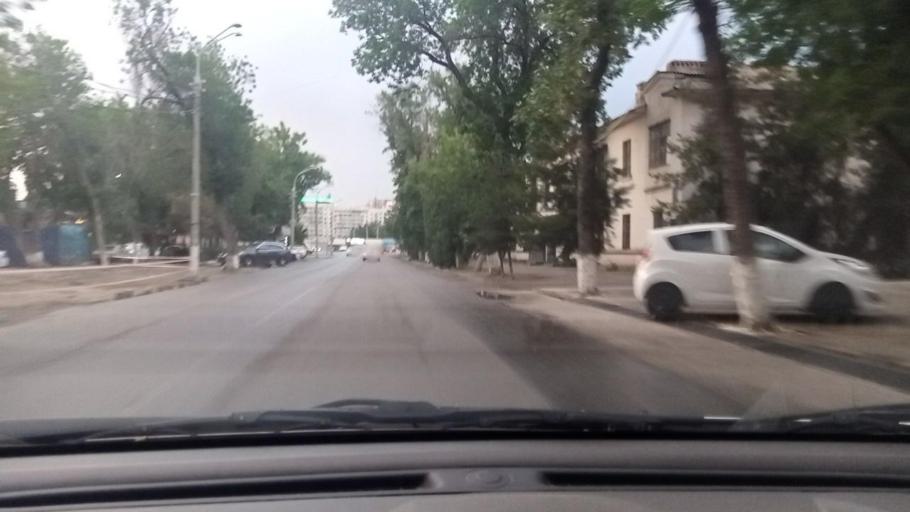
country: UZ
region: Toshkent Shahri
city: Tashkent
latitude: 41.2857
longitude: 69.2834
